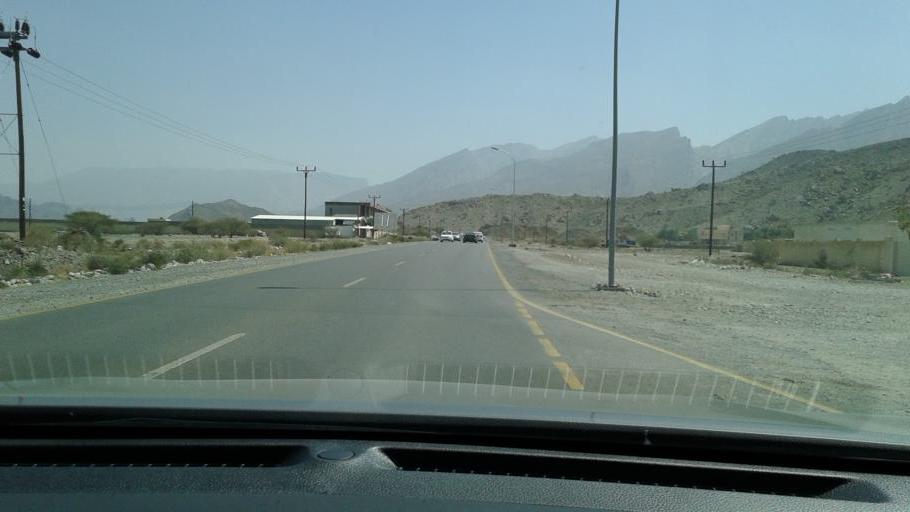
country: OM
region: Al Batinah
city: Rustaq
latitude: 23.3754
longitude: 57.4530
